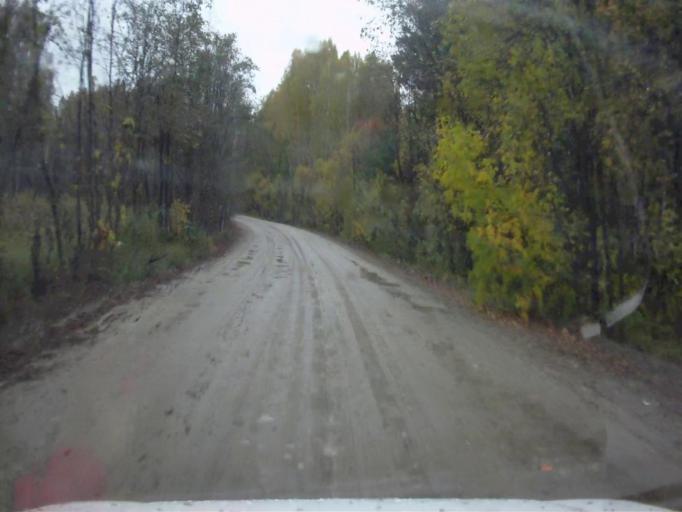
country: RU
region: Chelyabinsk
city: Kyshtym
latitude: 55.8279
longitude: 60.4870
